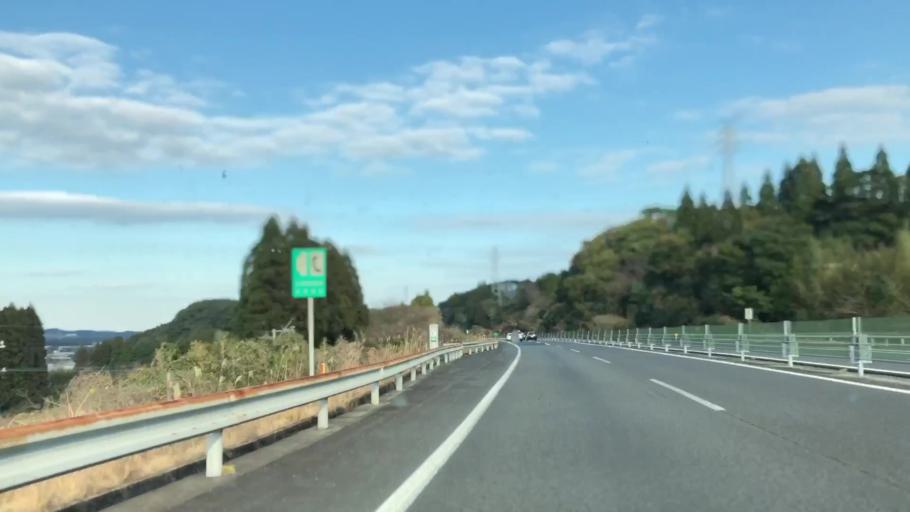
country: JP
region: Miyazaki
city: Miyazaki-shi
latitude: 31.8343
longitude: 131.3407
